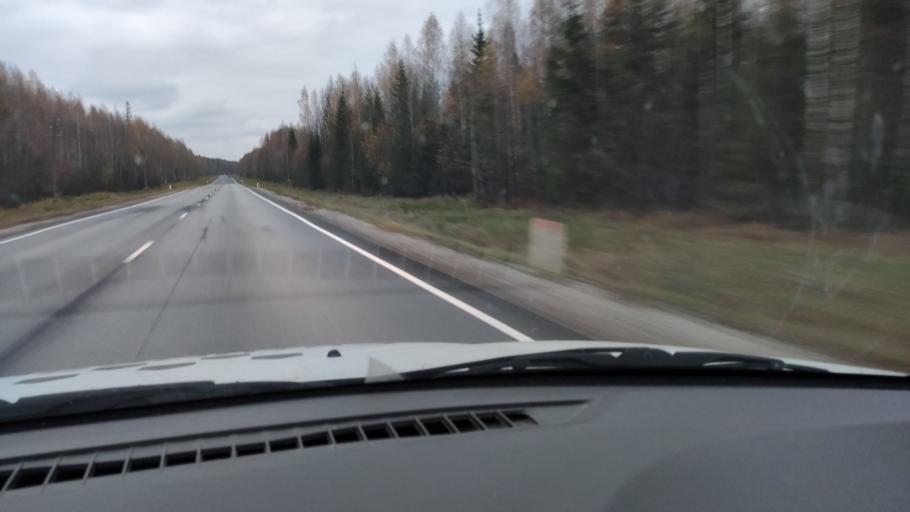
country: RU
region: Kirov
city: Kostino
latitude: 58.8166
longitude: 52.9525
